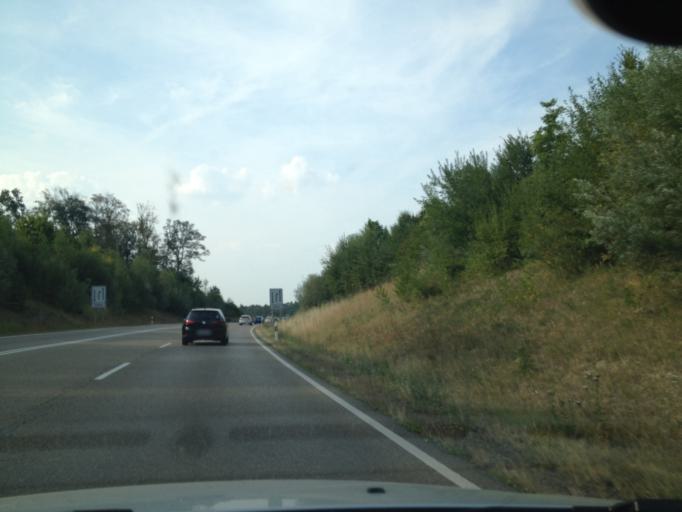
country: DE
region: Bavaria
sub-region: Swabia
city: Kaisheim
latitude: 48.7678
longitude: 10.7765
